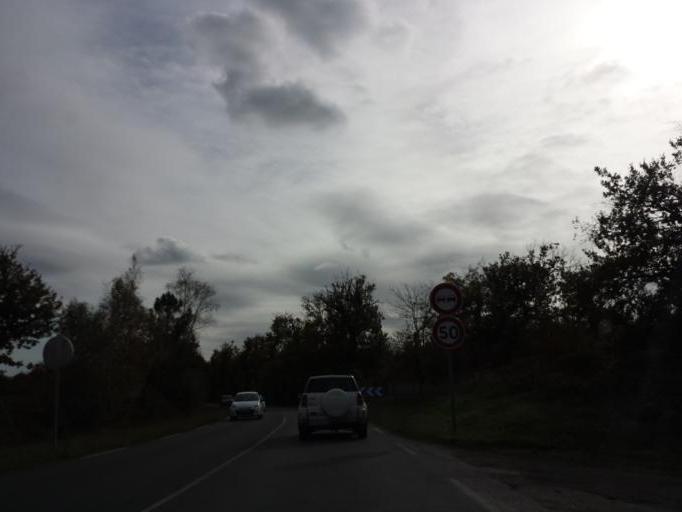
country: FR
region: Aquitaine
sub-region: Departement de la Gironde
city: Marcheprime
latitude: 44.7803
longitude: -0.9318
